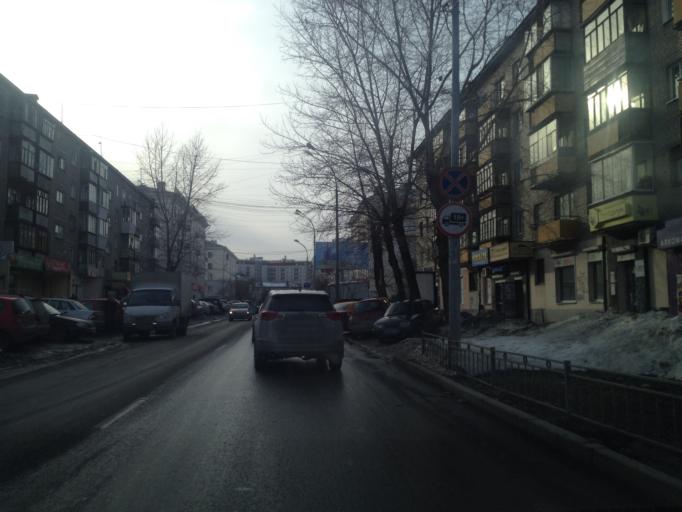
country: RU
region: Sverdlovsk
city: Yekaterinburg
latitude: 56.8541
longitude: 60.6074
